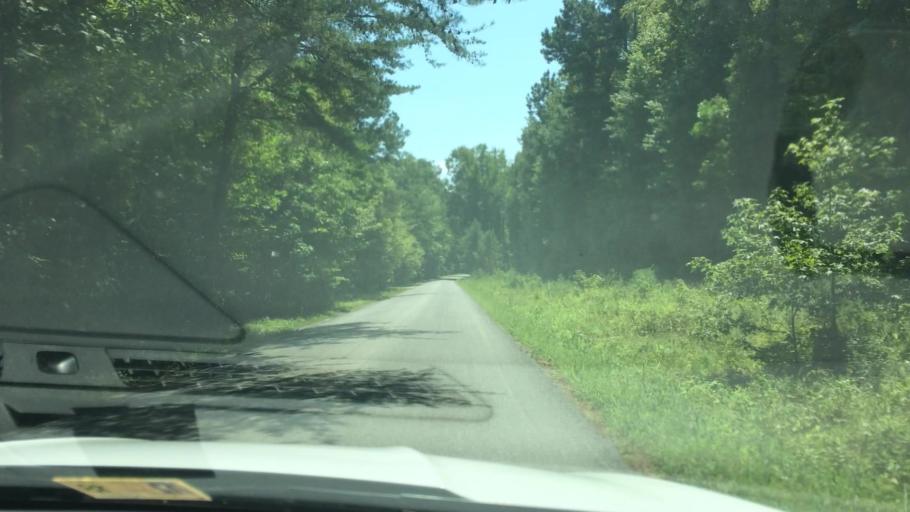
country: US
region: Virginia
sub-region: Charles City County
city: Charles City
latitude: 37.2855
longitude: -76.9641
